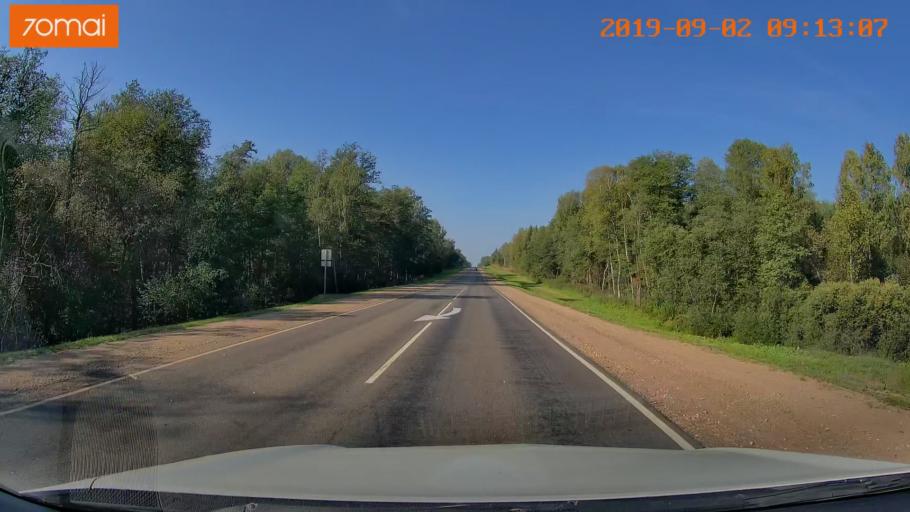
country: RU
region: Kaluga
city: Nikola-Lenivets
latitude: 54.8558
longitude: 35.5423
